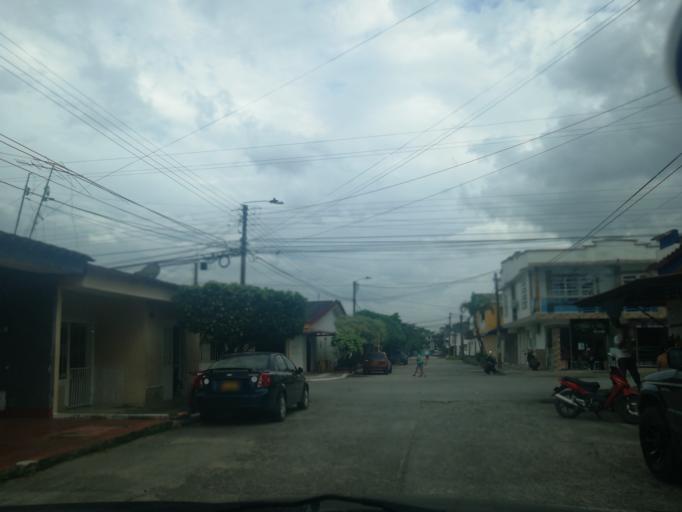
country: CO
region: Meta
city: Acacias
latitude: 3.9851
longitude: -73.7700
